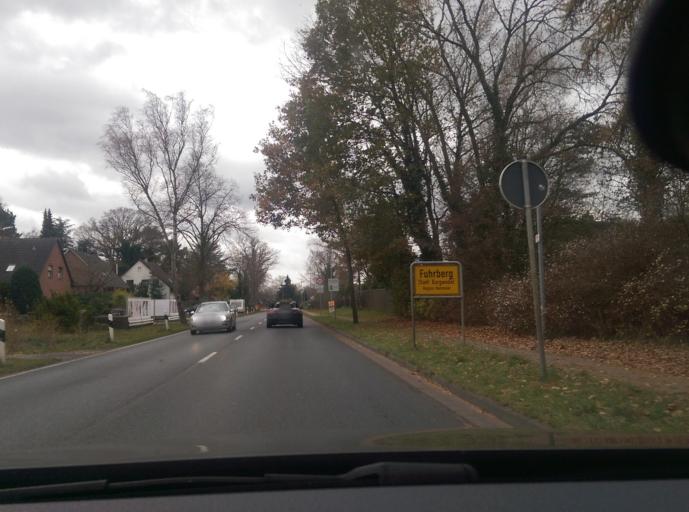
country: DE
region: Lower Saxony
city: Wietze
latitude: 52.5696
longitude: 9.8573
